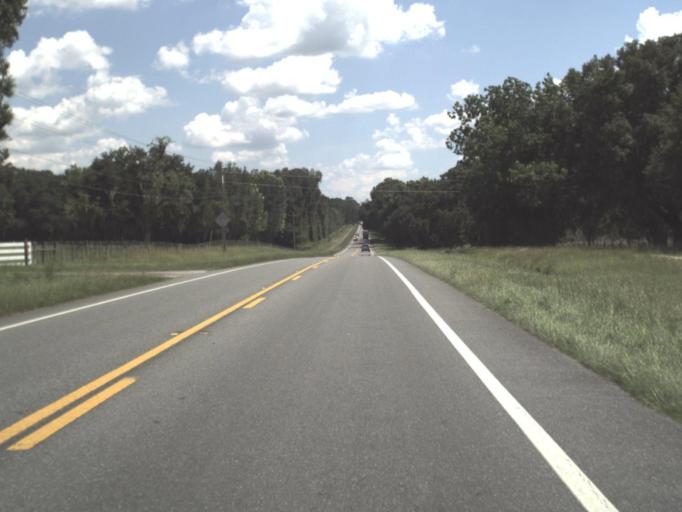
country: US
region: Florida
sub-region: Columbia County
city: Watertown
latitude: 30.0756
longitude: -82.6008
